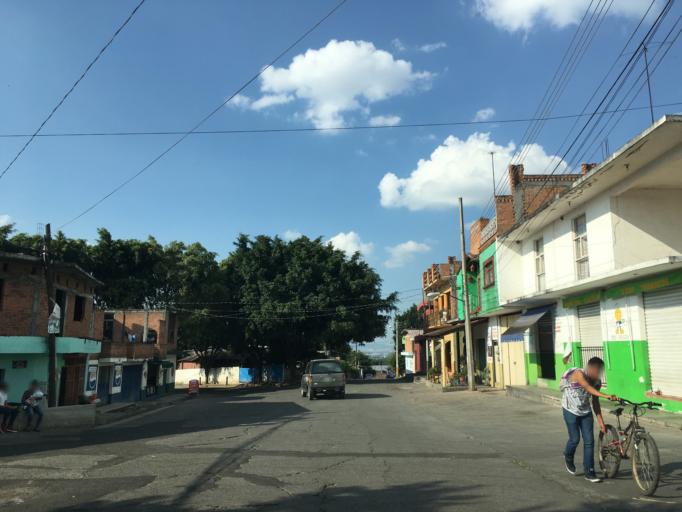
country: MX
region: Michoacan
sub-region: Morelia
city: Morelos
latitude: 19.6477
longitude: -101.2370
